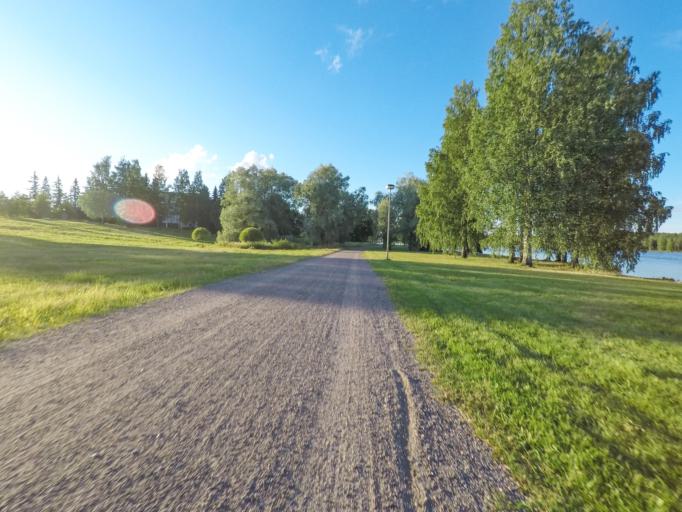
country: FI
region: South Karelia
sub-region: Imatra
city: Imatra
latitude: 61.1895
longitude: 28.7808
